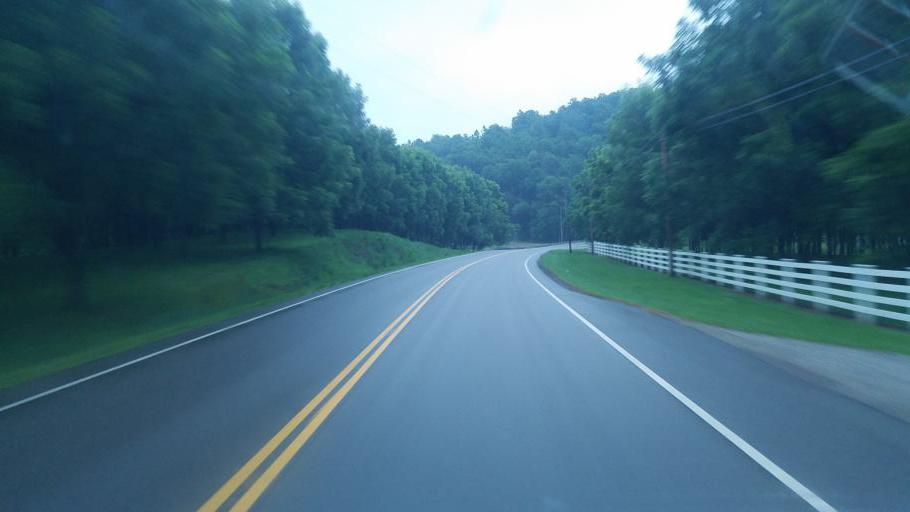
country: US
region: Ohio
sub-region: Coshocton County
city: Coshocton
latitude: 40.3423
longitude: -82.0505
